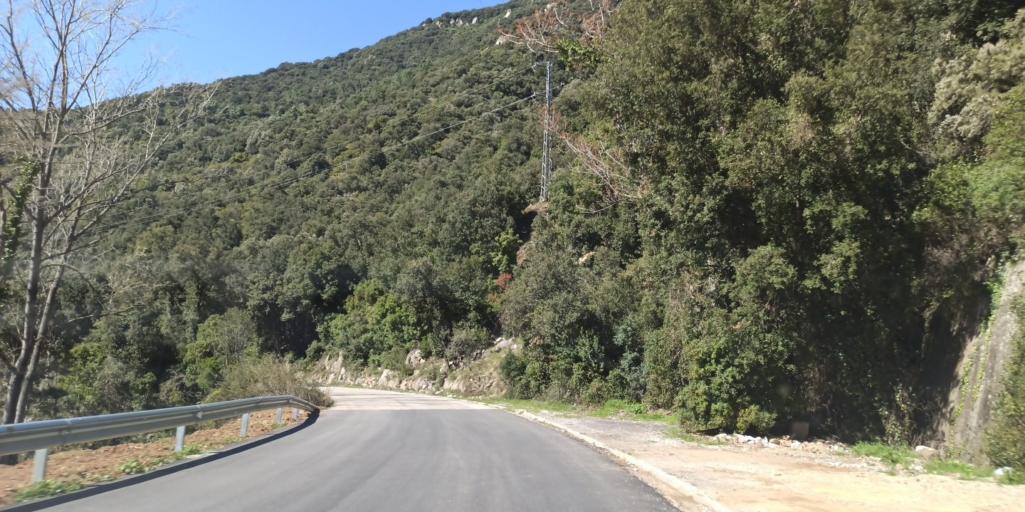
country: ES
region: Catalonia
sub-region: Provincia de Girona
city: Susqueda
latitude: 41.9926
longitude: 2.5693
